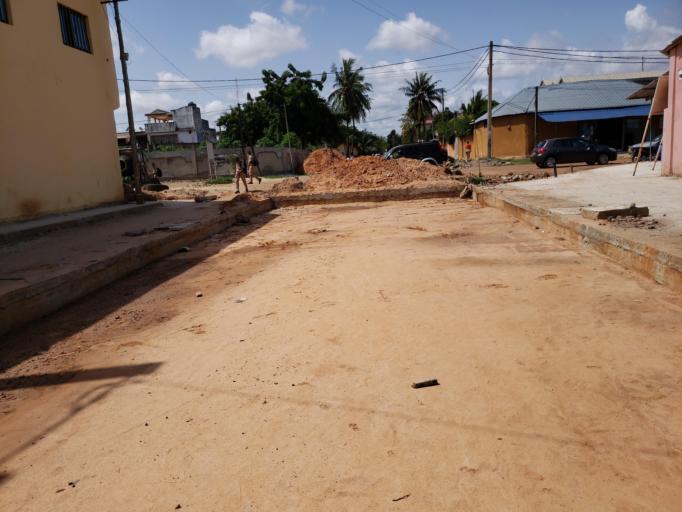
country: TG
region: Maritime
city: Lome
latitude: 6.1941
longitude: 1.1923
